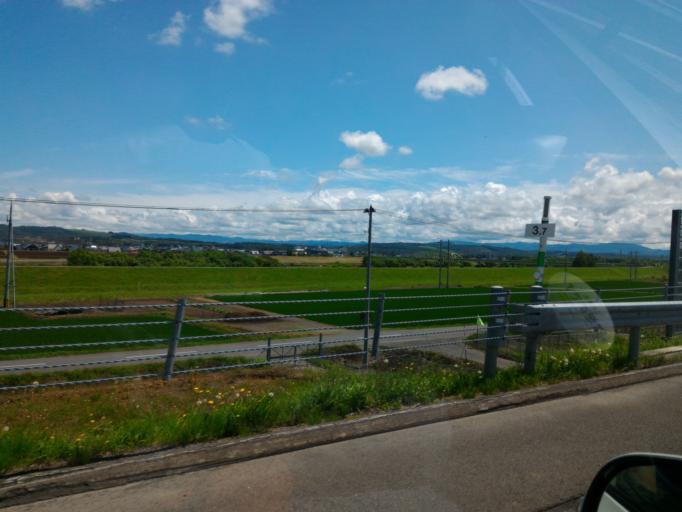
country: JP
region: Hokkaido
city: Nayoro
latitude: 44.3505
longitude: 142.4357
